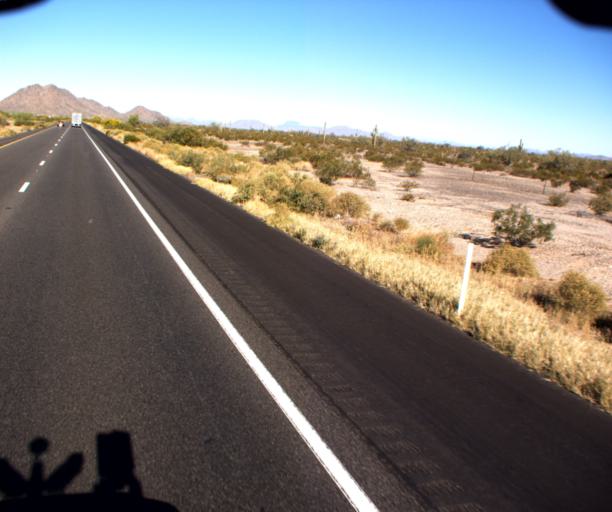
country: US
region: Arizona
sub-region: Maricopa County
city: Gila Bend
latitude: 32.9005
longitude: -112.5139
